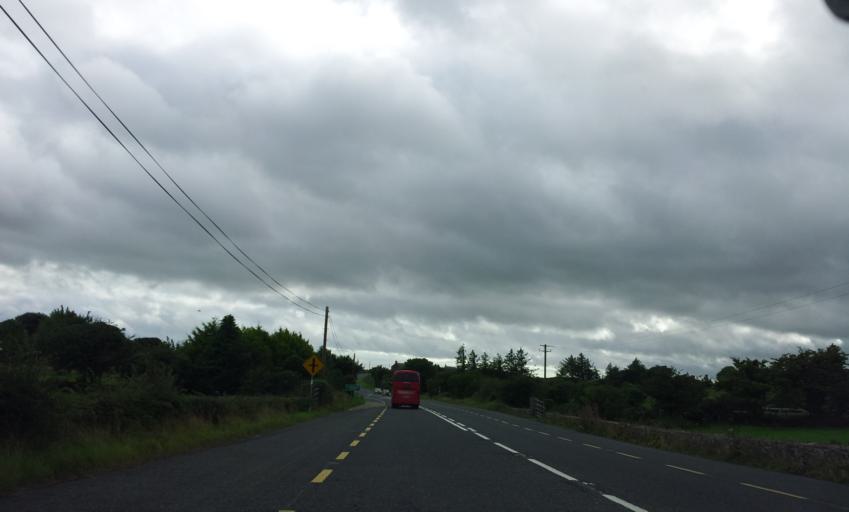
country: IE
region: Munster
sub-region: County Cork
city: Youghal
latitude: 51.9971
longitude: -7.7280
